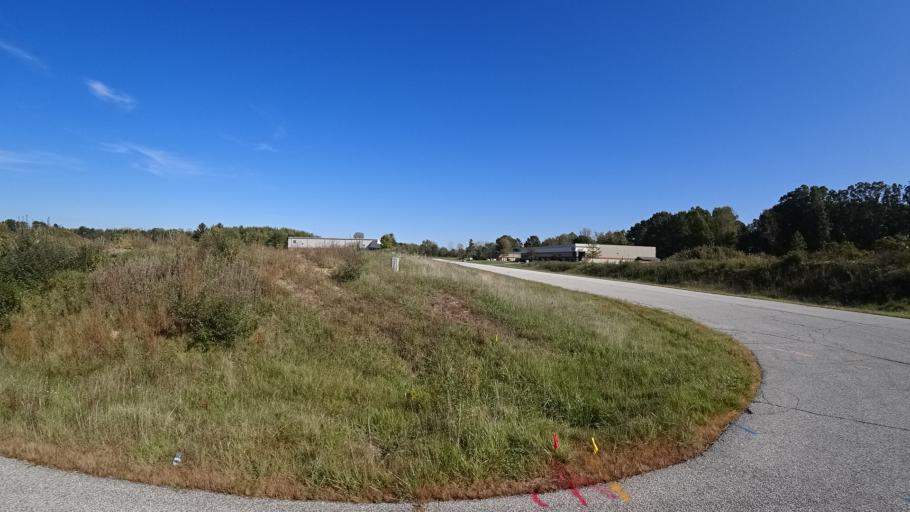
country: US
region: Indiana
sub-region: LaPorte County
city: Trail Creek
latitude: 41.6963
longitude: -86.8421
